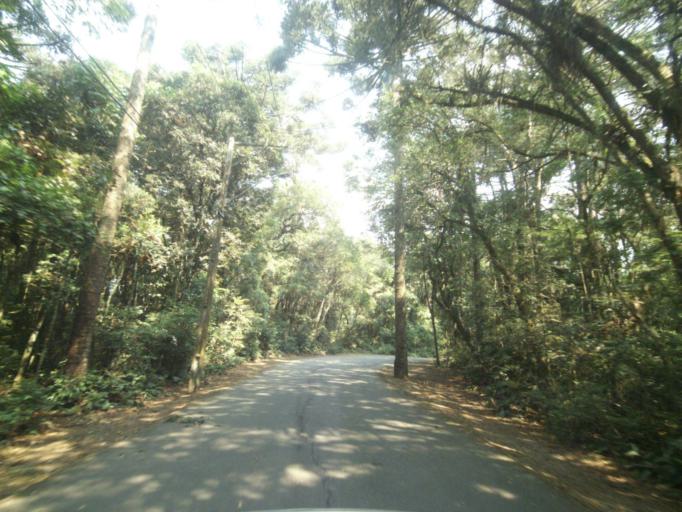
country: BR
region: Parana
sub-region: Sao Jose Dos Pinhais
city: Sao Jose dos Pinhais
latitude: -25.5551
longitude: -49.2329
